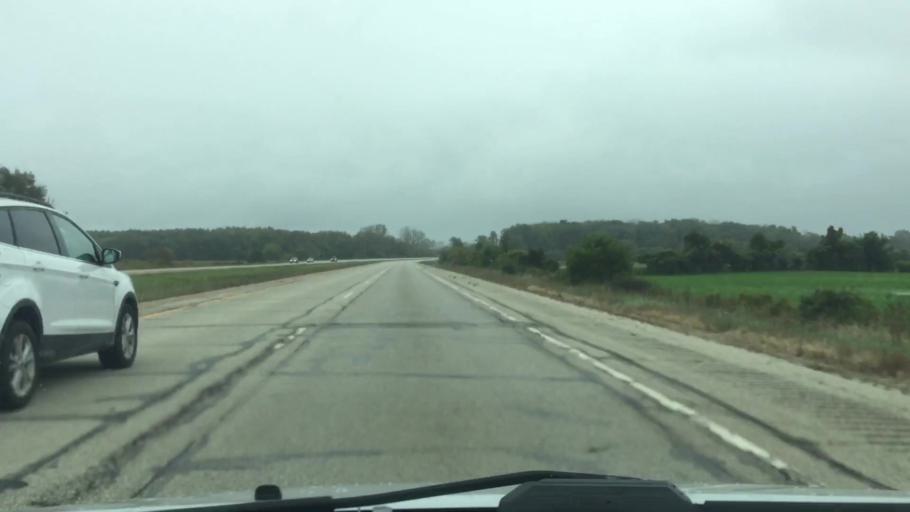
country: US
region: Wisconsin
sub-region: Walworth County
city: Como
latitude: 42.6364
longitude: -88.4818
